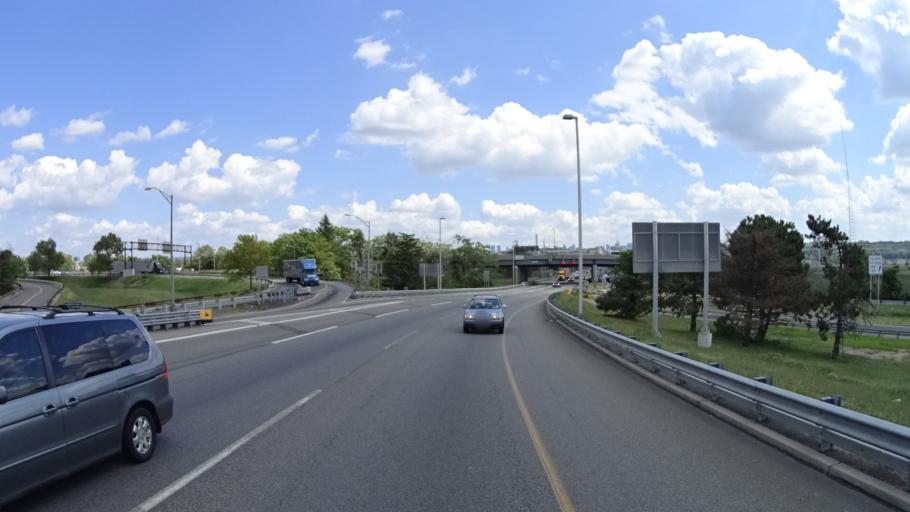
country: US
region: New Jersey
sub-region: Hudson County
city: Secaucus
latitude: 40.7809
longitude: -74.0544
